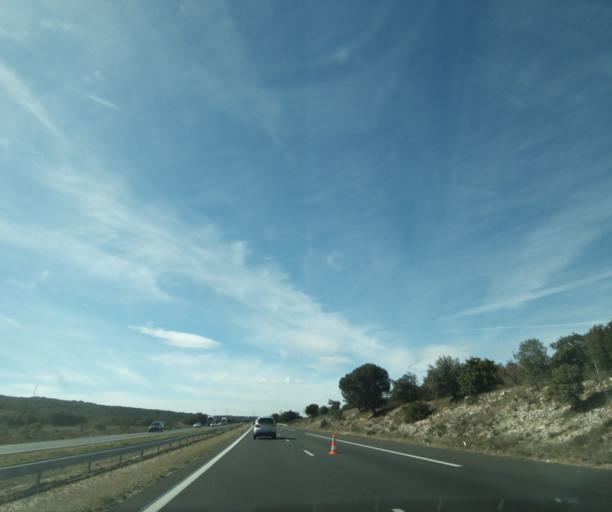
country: FR
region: Languedoc-Roussillon
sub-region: Departement du Gard
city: Saze
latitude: 43.9706
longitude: 4.6470
